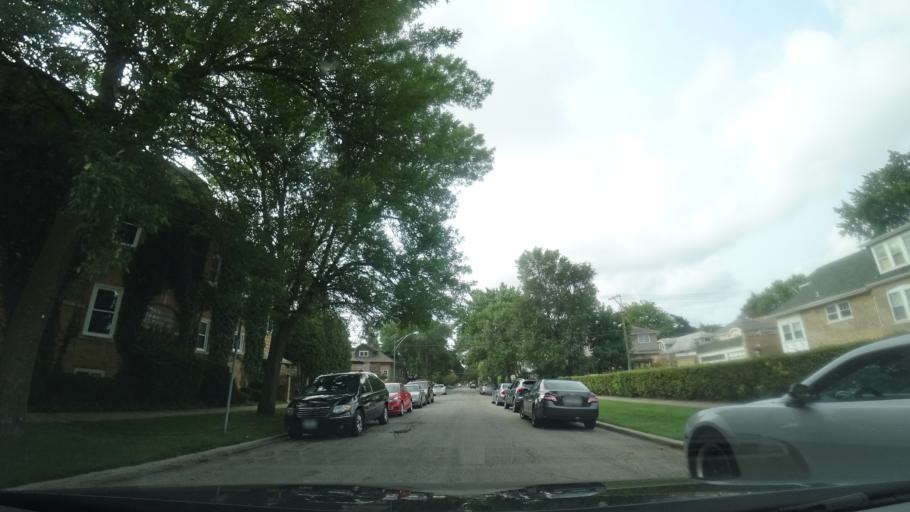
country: US
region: Illinois
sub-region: Cook County
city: Lincolnwood
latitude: 42.0076
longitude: -87.6975
